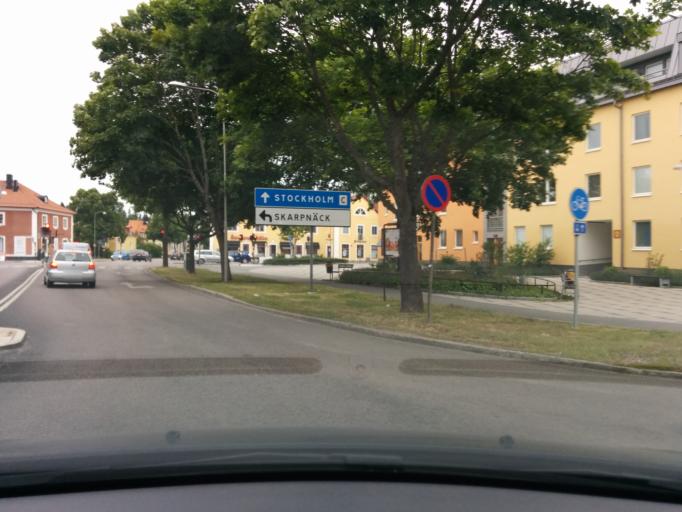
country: SE
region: Stockholm
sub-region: Stockholms Kommun
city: Arsta
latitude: 59.2802
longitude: 18.1098
